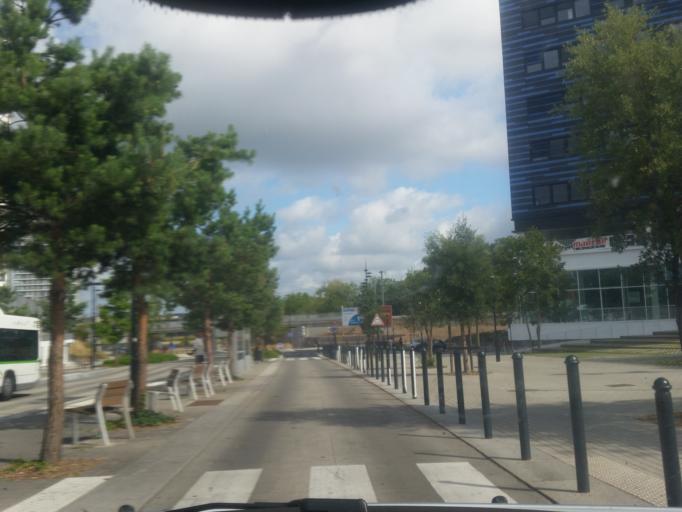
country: FR
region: Pays de la Loire
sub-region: Departement de la Loire-Atlantique
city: Nantes
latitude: 47.2143
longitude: -1.5297
